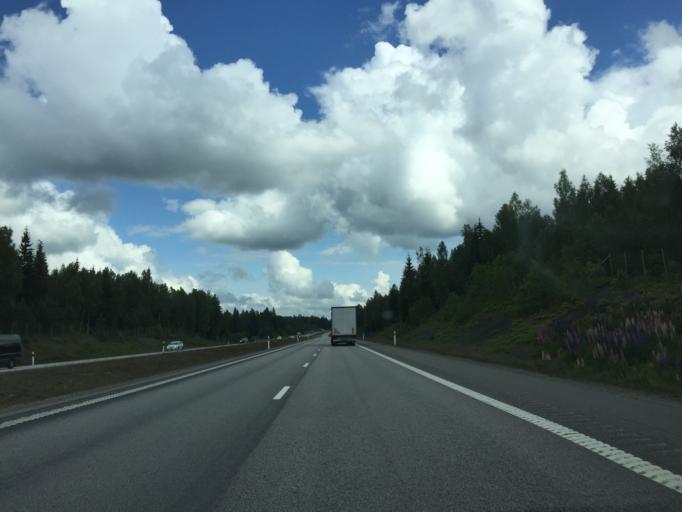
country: SE
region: OErebro
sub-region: Lindesbergs Kommun
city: Fellingsbro
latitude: 59.3585
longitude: 15.5678
